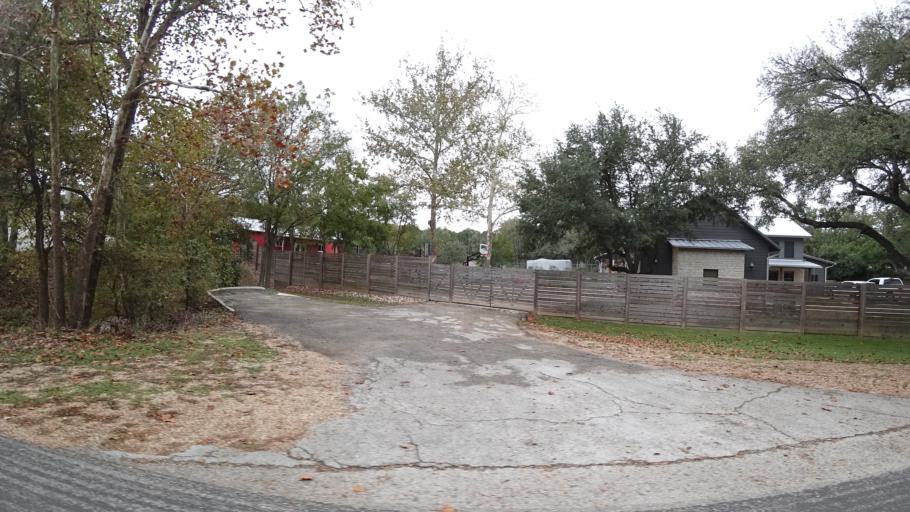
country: US
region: Texas
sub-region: Travis County
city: Barton Creek
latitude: 30.2348
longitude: -97.9002
